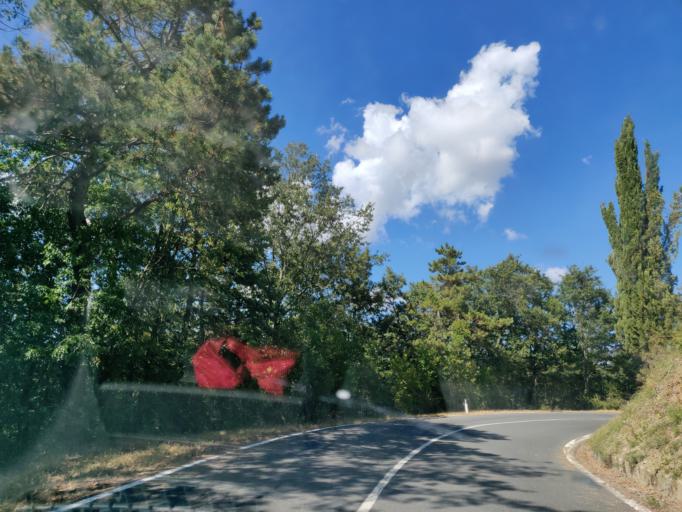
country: IT
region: Tuscany
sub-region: Provincia di Siena
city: Abbadia San Salvatore
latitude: 42.9106
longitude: 11.6901
